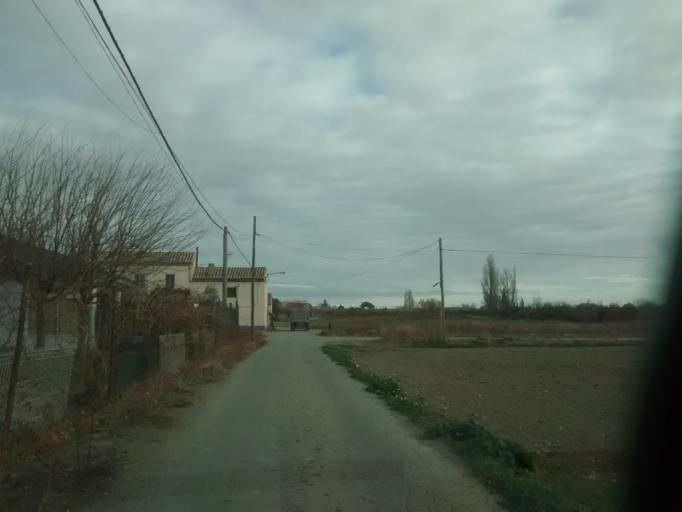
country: ES
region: Aragon
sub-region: Provincia de Zaragoza
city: Villanueva de Gallego
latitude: 41.7023
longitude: -0.8218
